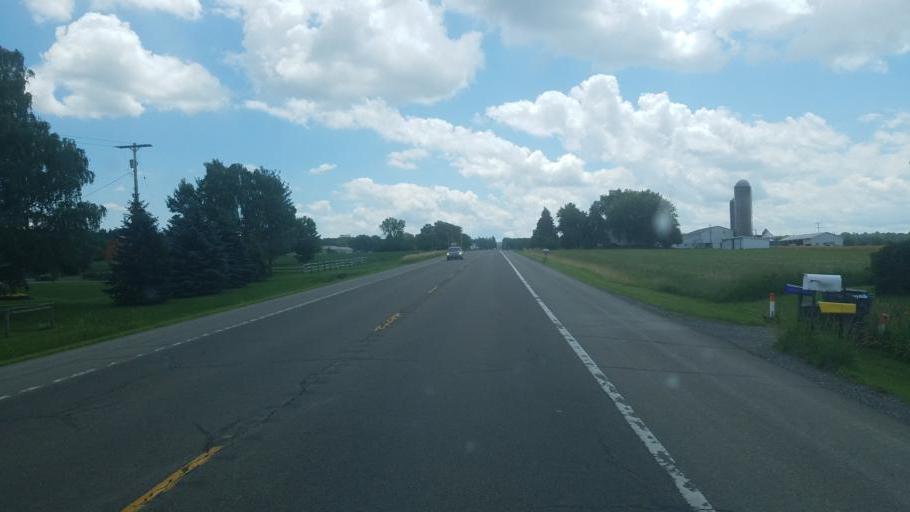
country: US
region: New York
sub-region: Yates County
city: Penn Yan
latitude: 42.6091
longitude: -77.0382
